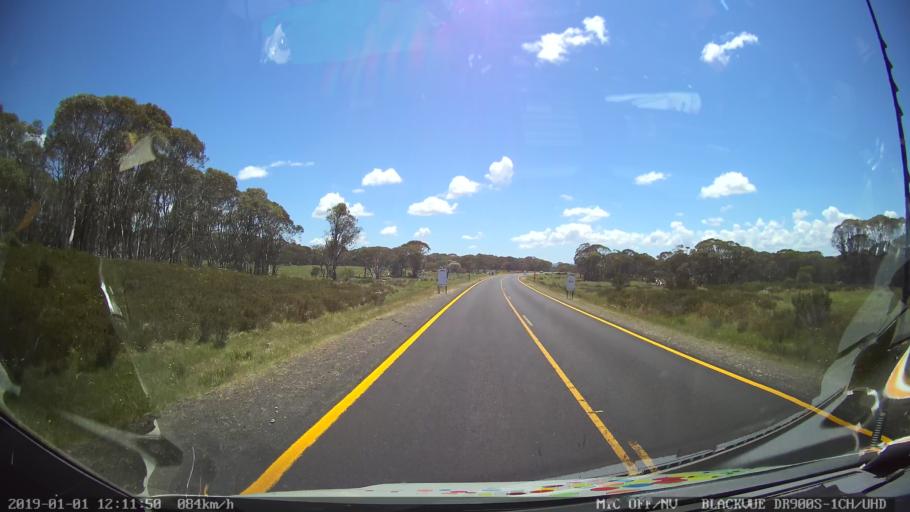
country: AU
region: New South Wales
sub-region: Tumut Shire
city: Tumut
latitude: -35.7793
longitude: 148.5095
